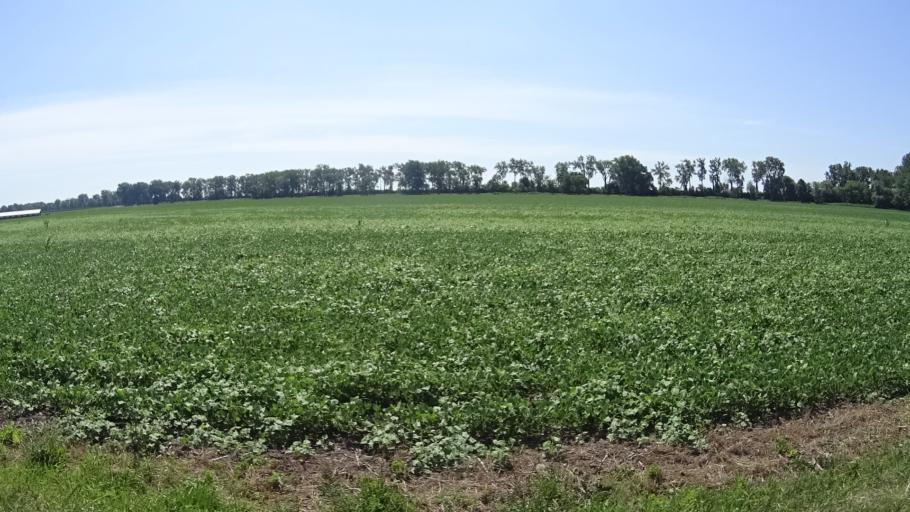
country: US
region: Ohio
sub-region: Erie County
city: Sandusky
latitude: 41.4234
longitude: -82.8030
